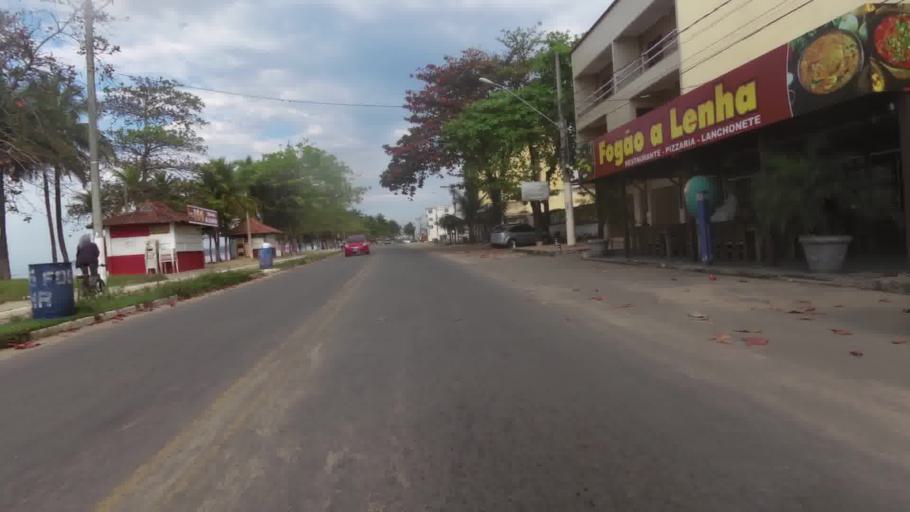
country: BR
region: Espirito Santo
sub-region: Piuma
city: Piuma
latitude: -20.8422
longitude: -40.7294
